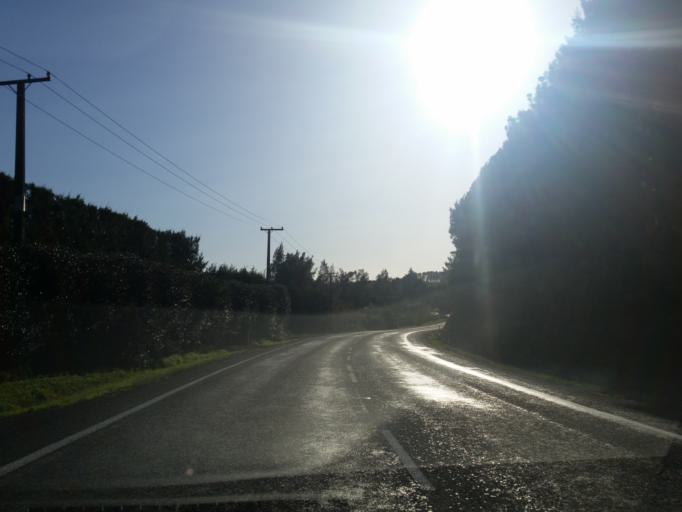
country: NZ
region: Bay of Plenty
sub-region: Western Bay of Plenty District
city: Katikati
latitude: -37.5359
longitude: 175.9125
